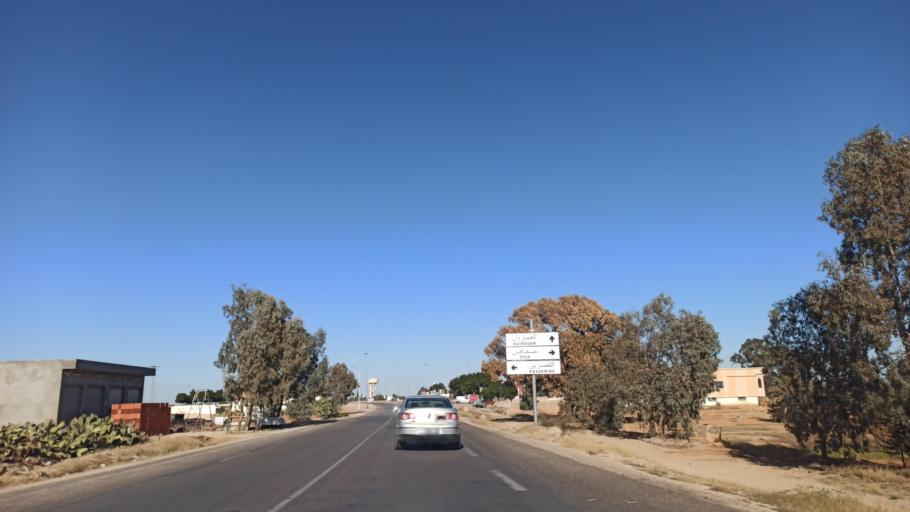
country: TN
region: Sidi Bu Zayd
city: Jilma
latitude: 35.1448
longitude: 9.3626
